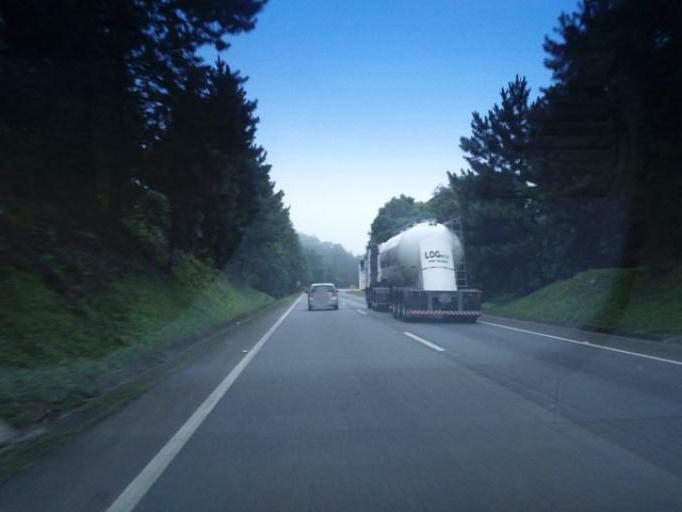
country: BR
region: Parana
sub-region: Sao Jose Dos Pinhais
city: Sao Jose dos Pinhais
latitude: -25.8535
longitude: -49.0222
